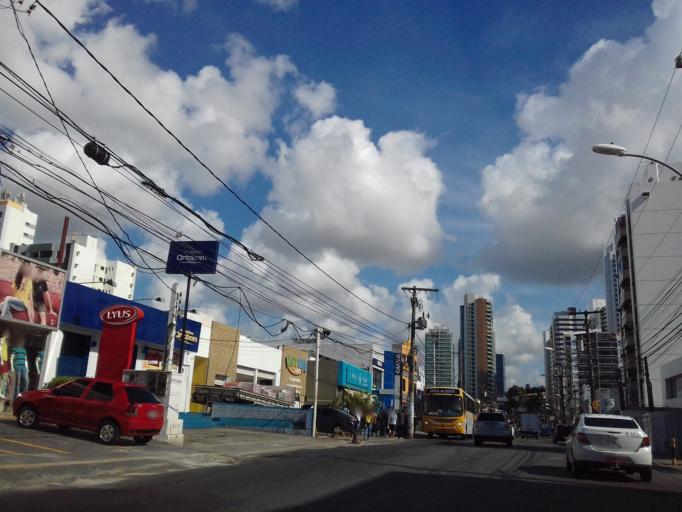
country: BR
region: Bahia
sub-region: Salvador
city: Salvador
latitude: -12.9933
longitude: -38.4547
